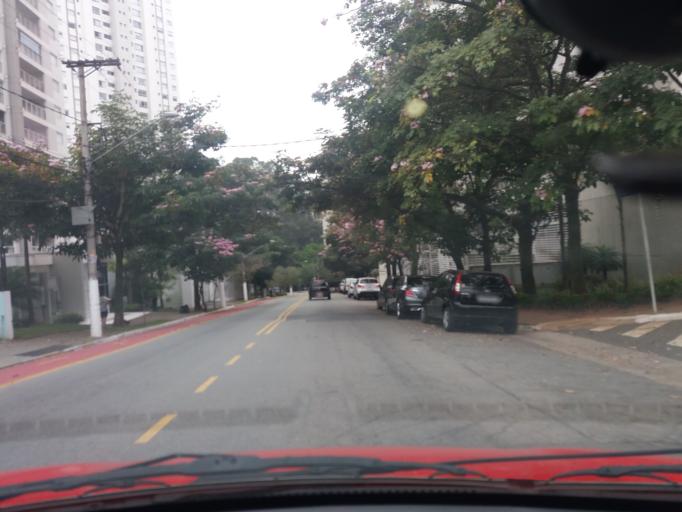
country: BR
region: Sao Paulo
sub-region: Taboao Da Serra
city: Taboao da Serra
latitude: -23.6296
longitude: -46.7404
